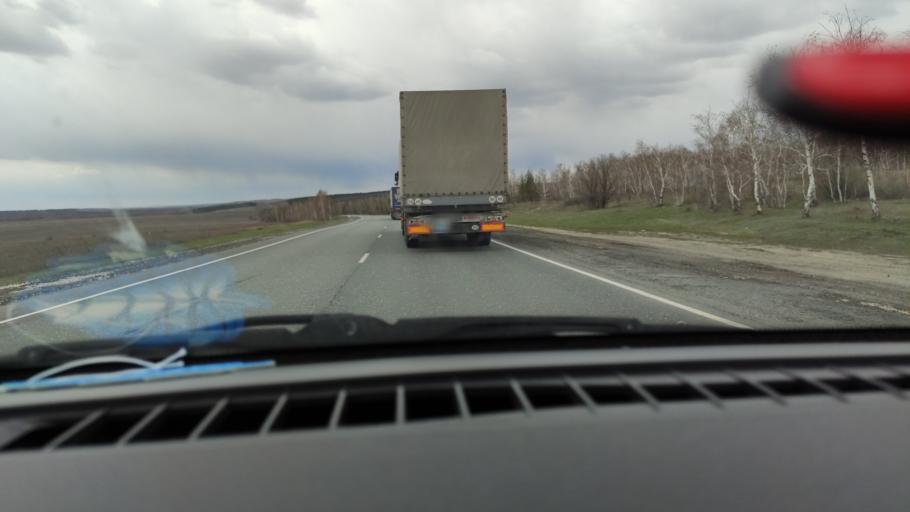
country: RU
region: Saratov
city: Sennoy
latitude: 52.1309
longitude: 46.8615
